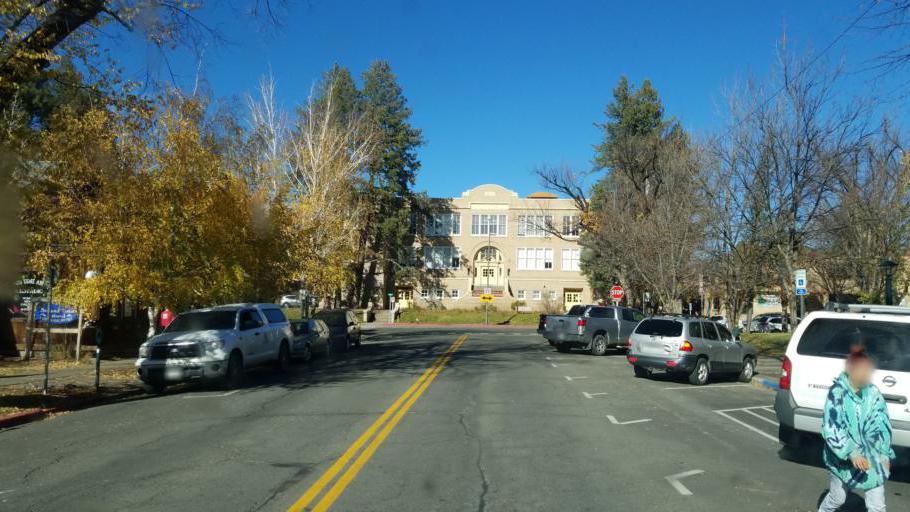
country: US
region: Colorado
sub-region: La Plata County
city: Durango
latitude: 37.2759
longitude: -107.8785
